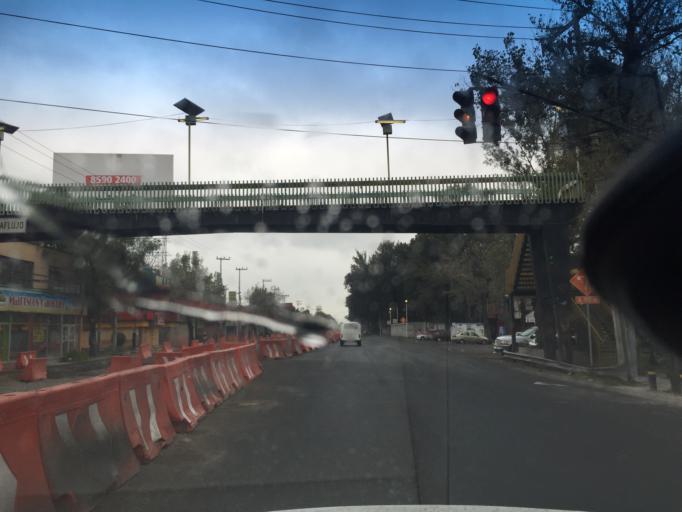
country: MX
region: Mexico
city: Colonia Lindavista
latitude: 19.4940
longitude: -99.1487
